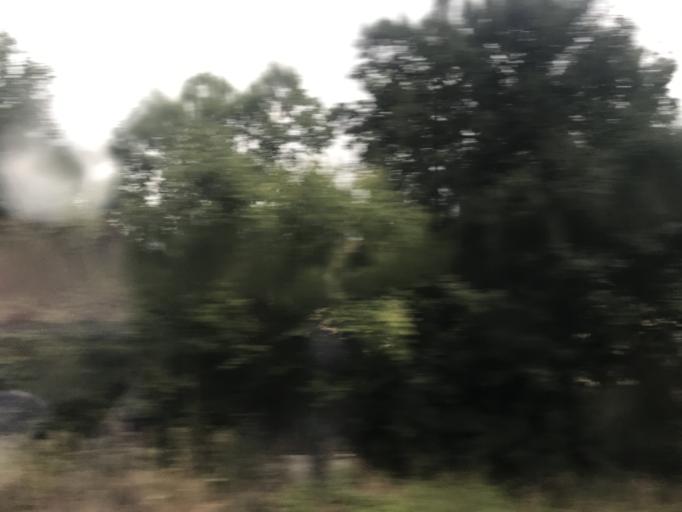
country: DE
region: Bavaria
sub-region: Regierungsbezirk Unterfranken
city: Rottendorf
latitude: 49.8157
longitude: 10.0625
